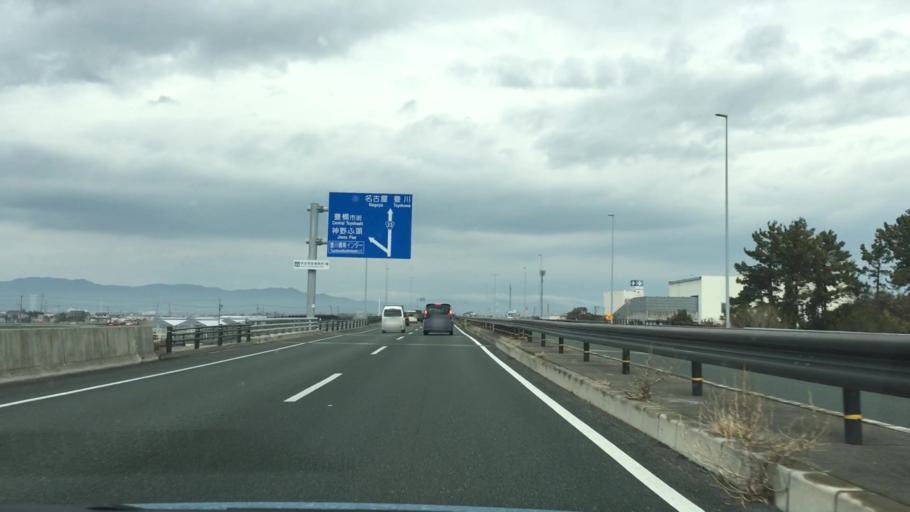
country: JP
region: Aichi
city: Kozakai-cho
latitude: 34.7571
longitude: 137.3338
